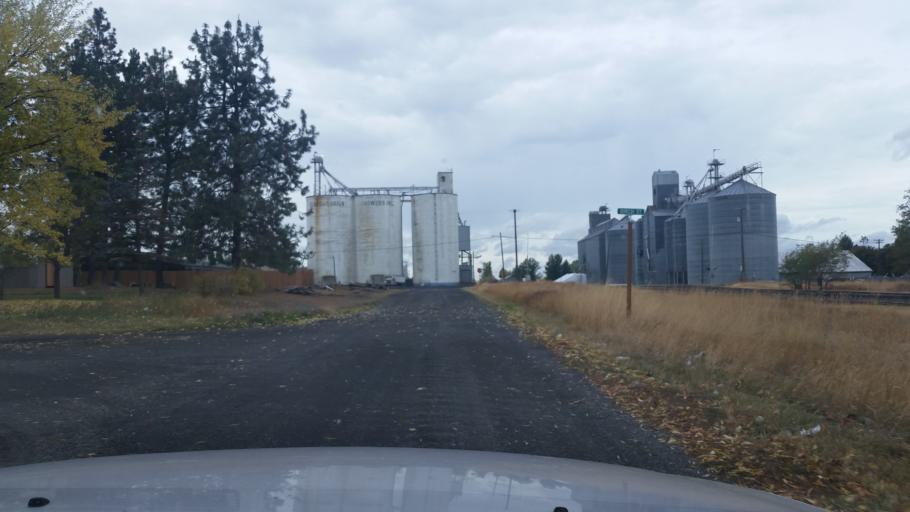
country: US
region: Washington
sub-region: Spokane County
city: Medical Lake
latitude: 47.6705
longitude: -117.8762
